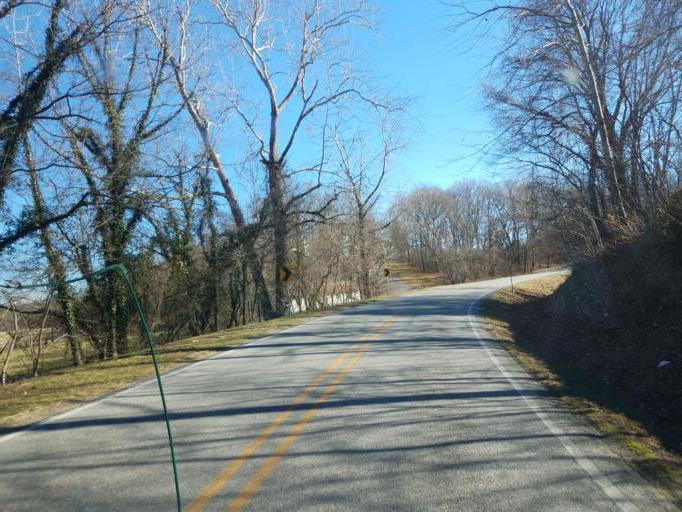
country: US
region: Arkansas
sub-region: Washington County
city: Elkins
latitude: 36.0319
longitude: -93.9426
